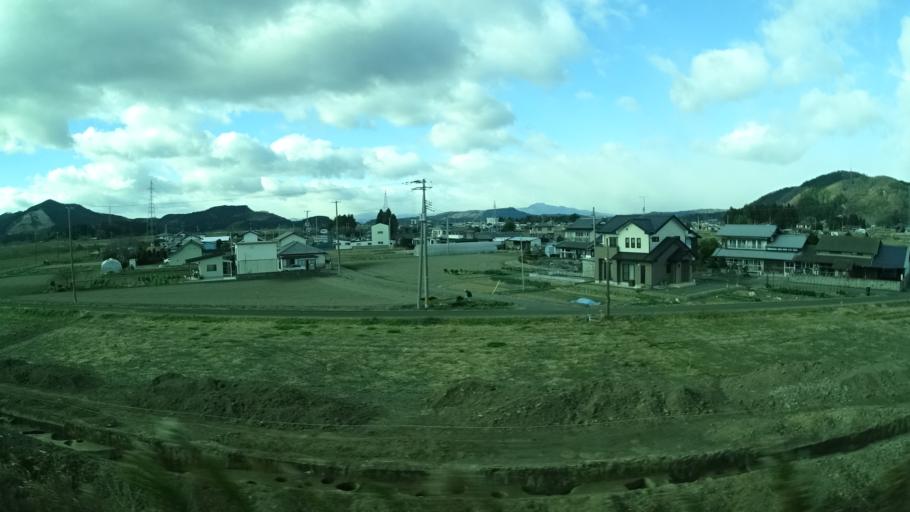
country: JP
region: Miyagi
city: Iwanuma
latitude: 38.0848
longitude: 140.8524
